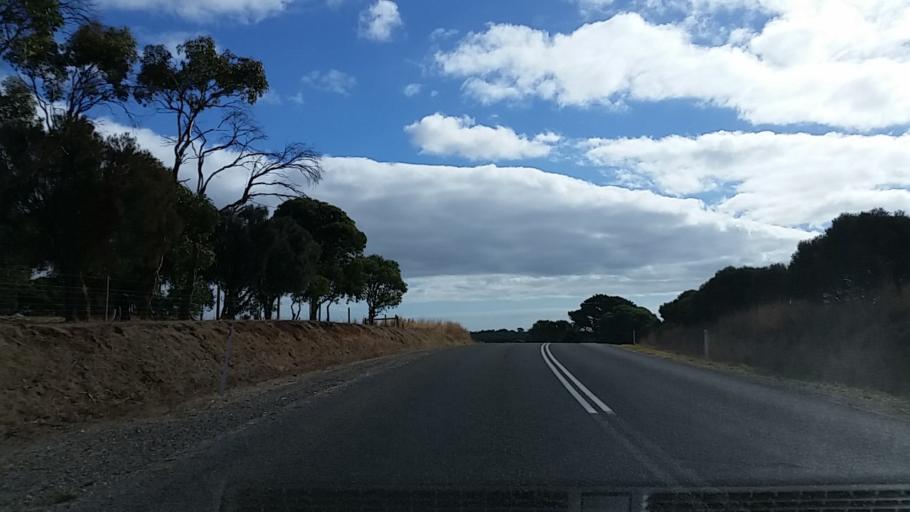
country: AU
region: South Australia
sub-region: Yankalilla
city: Normanville
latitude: -35.4134
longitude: 138.3621
